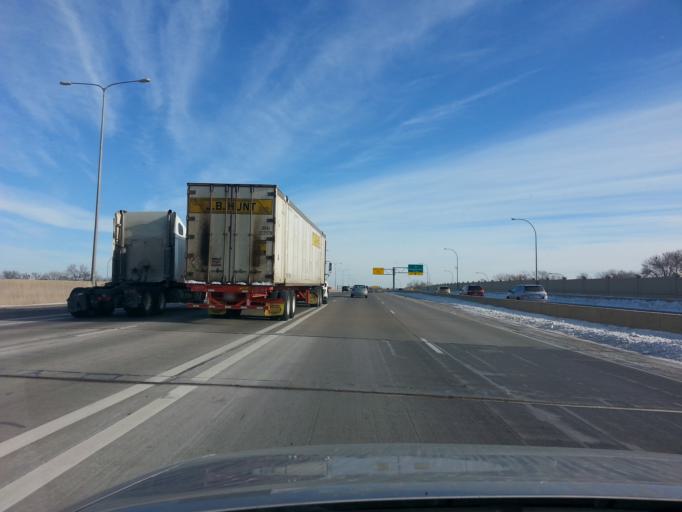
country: US
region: Minnesota
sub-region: Hennepin County
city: Richfield
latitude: 44.8900
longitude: -93.2883
